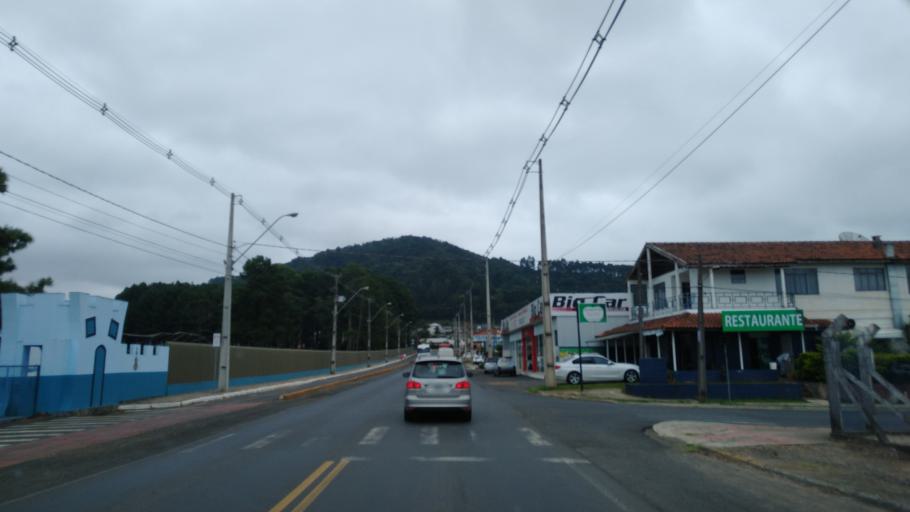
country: BR
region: Santa Catarina
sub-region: Porto Uniao
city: Porto Uniao
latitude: -26.2571
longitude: -51.0696
